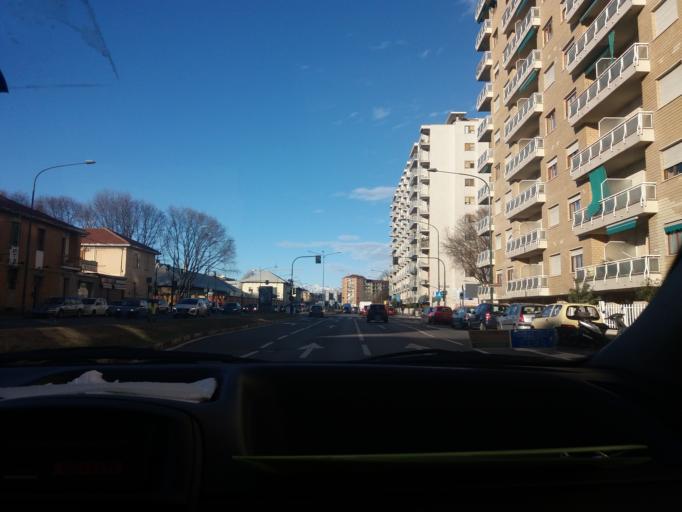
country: IT
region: Piedmont
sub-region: Provincia di Torino
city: Lesna
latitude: 45.0497
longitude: 7.6297
